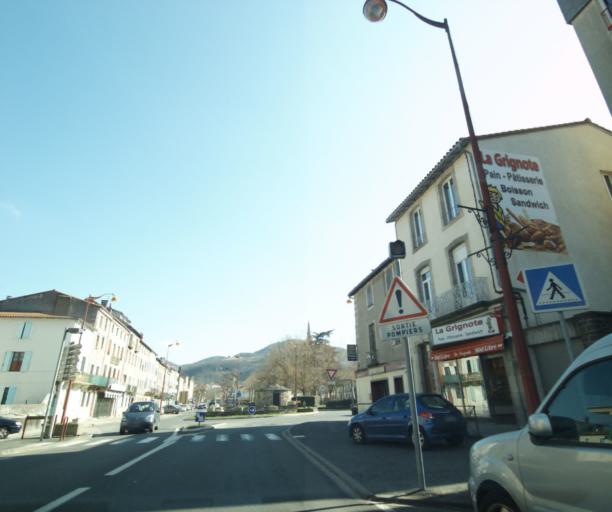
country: FR
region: Midi-Pyrenees
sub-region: Departement de l'Aveyron
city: Saint-Affrique
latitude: 43.9575
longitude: 2.8810
